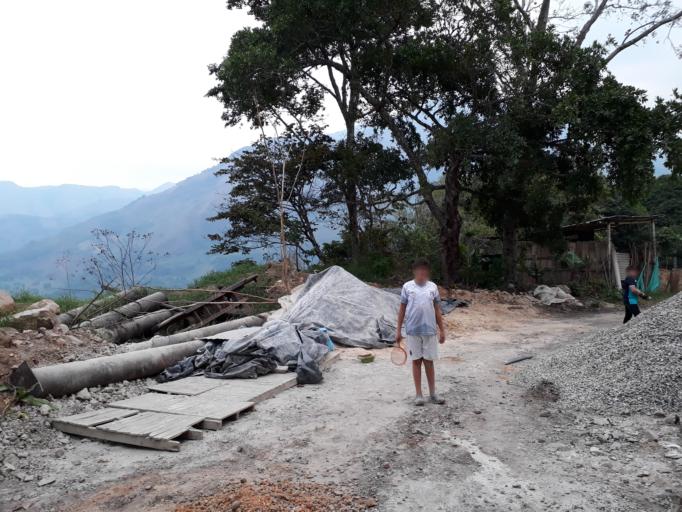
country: CO
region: Casanare
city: Nunchia
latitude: 5.6240
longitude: -72.4232
